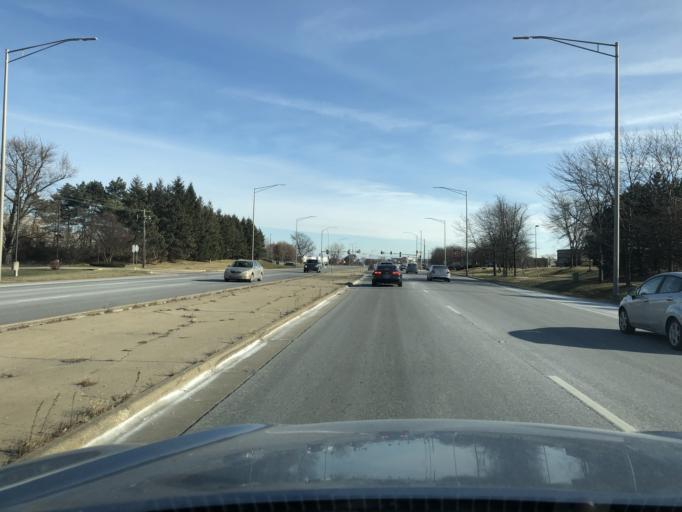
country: US
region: Illinois
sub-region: Lake County
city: Grandwood Park
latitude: 42.3855
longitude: -87.9687
